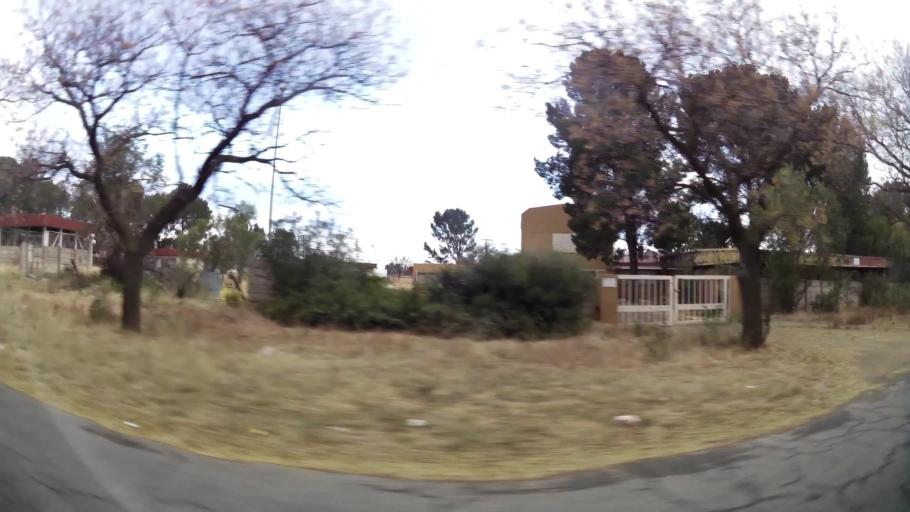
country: ZA
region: Orange Free State
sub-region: Lejweleputswa District Municipality
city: Welkom
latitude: -27.9618
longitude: 26.7141
